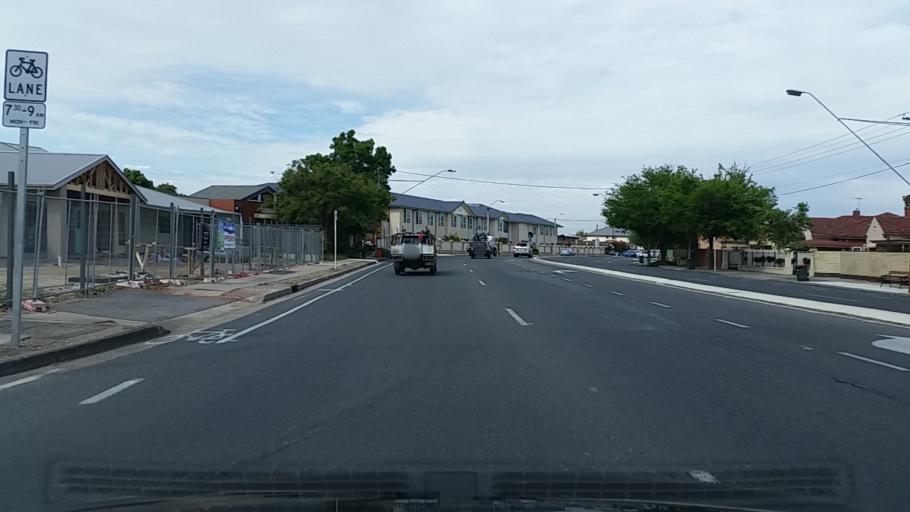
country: AU
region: South Australia
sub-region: City of West Torrens
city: Plympton
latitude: -34.9254
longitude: 138.5423
